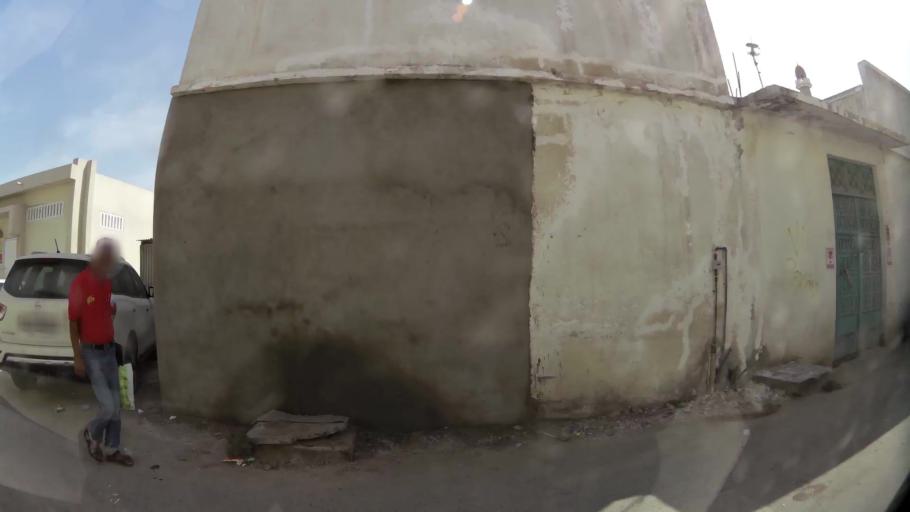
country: QA
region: Baladiyat ad Dawhah
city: Doha
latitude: 25.2804
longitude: 51.5327
